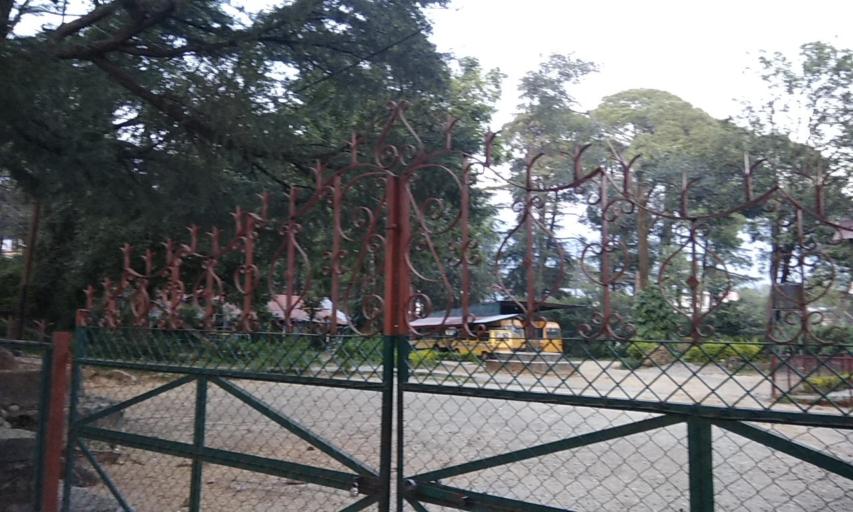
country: IN
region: Himachal Pradesh
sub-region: Kangra
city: Palampur
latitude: 32.1150
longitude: 76.5383
